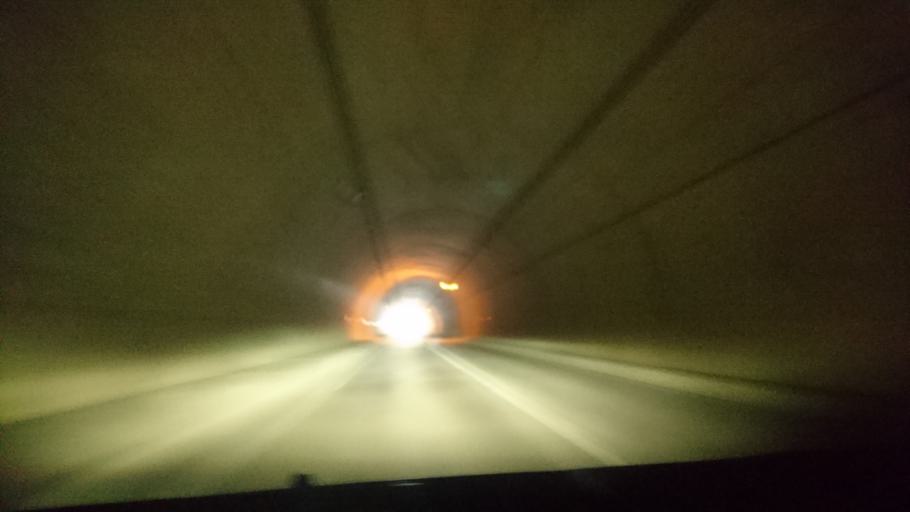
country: JP
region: Miyagi
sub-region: Oshika Gun
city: Onagawa Cho
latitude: 38.5859
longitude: 141.4805
